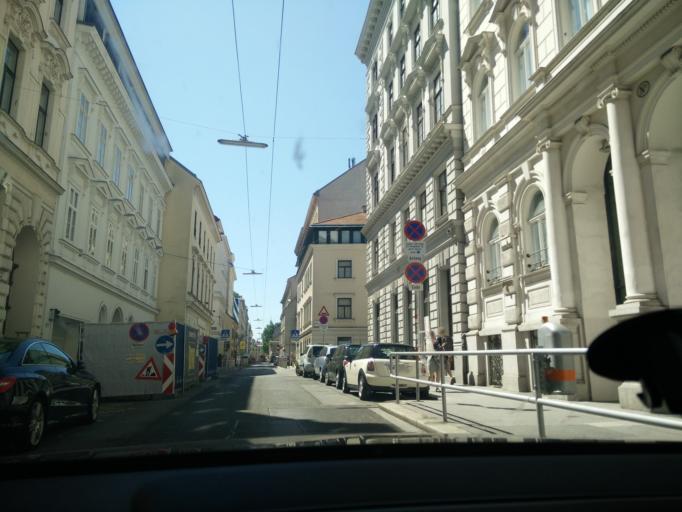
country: AT
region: Vienna
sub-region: Wien Stadt
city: Vienna
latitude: 48.2109
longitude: 16.3517
